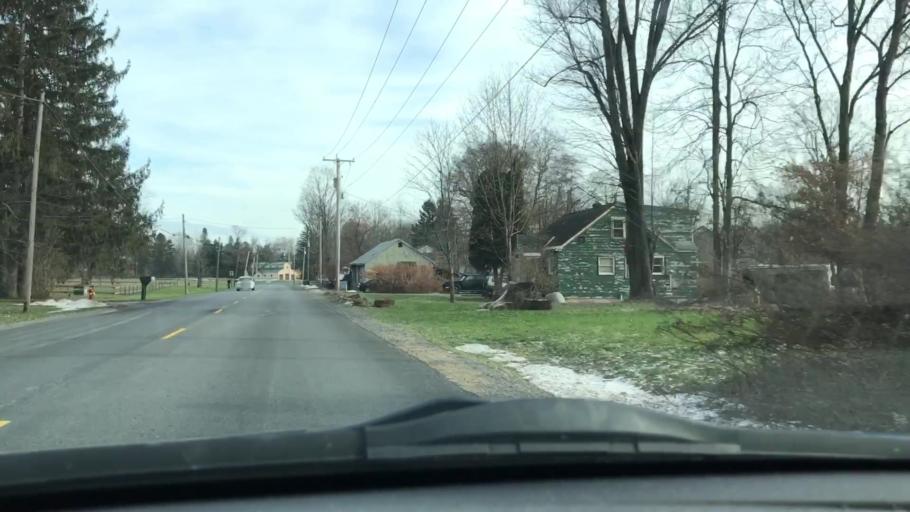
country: US
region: New York
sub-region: Madison County
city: Oneida
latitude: 43.0983
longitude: -75.6326
